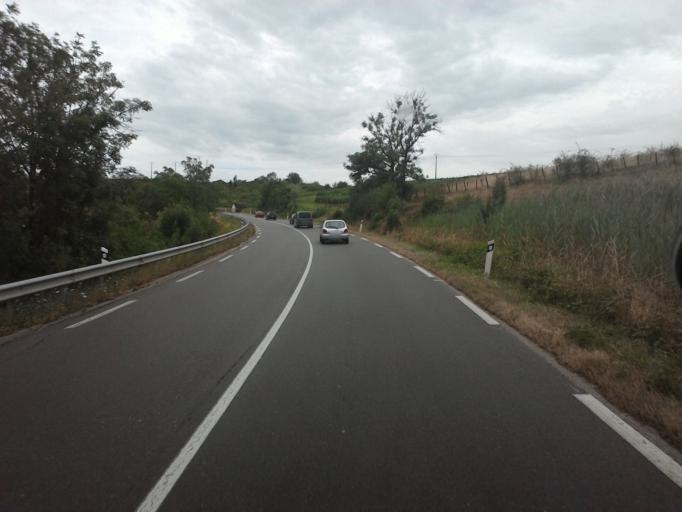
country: FR
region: Franche-Comte
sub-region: Departement du Jura
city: Poligny
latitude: 46.8819
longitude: 5.7218
